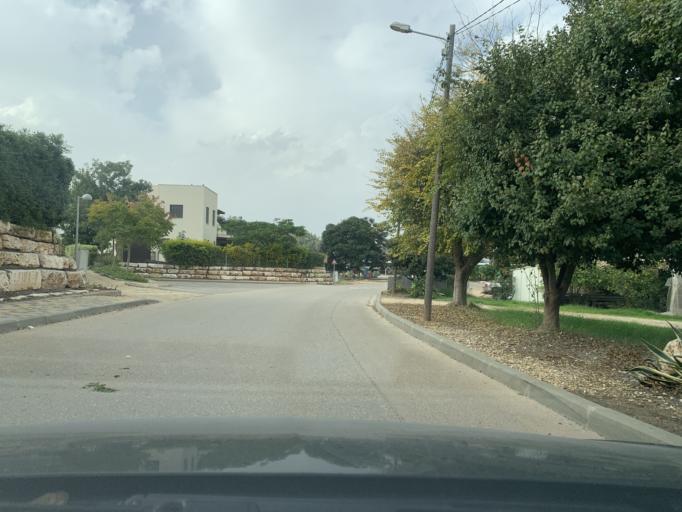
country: IL
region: Central District
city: Tirah
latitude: 32.2183
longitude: 34.9409
